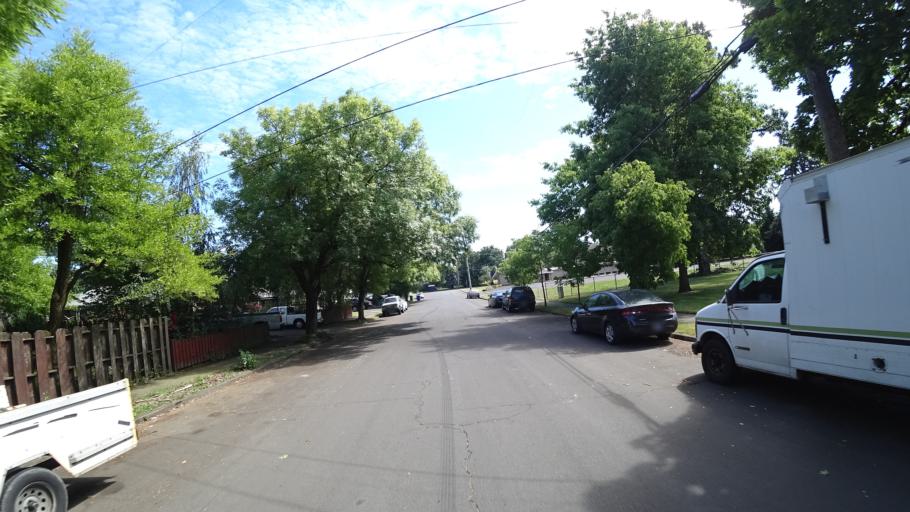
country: US
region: Washington
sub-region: Clark County
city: Vancouver
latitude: 45.5890
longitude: -122.7078
